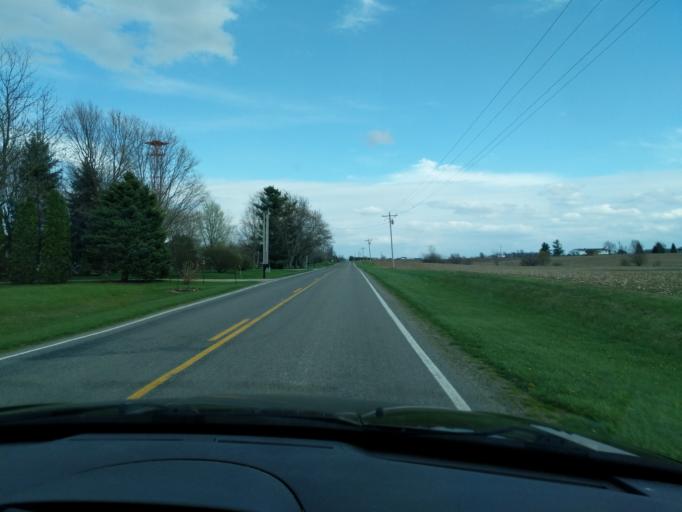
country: US
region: Ohio
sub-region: Champaign County
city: Urbana
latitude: 40.1537
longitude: -83.6517
